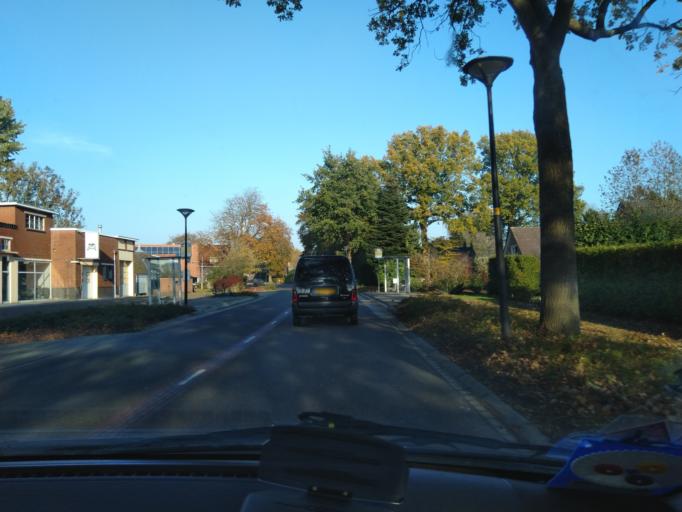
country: NL
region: Drenthe
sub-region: Gemeente Tynaarlo
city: Zuidlaren
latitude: 53.1091
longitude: 6.7088
